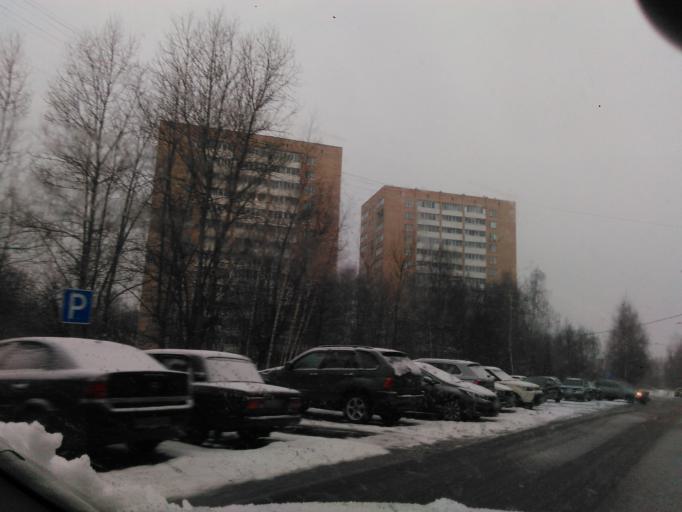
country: RU
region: Moskovskaya
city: Rzhavki
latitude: 55.9996
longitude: 37.2377
